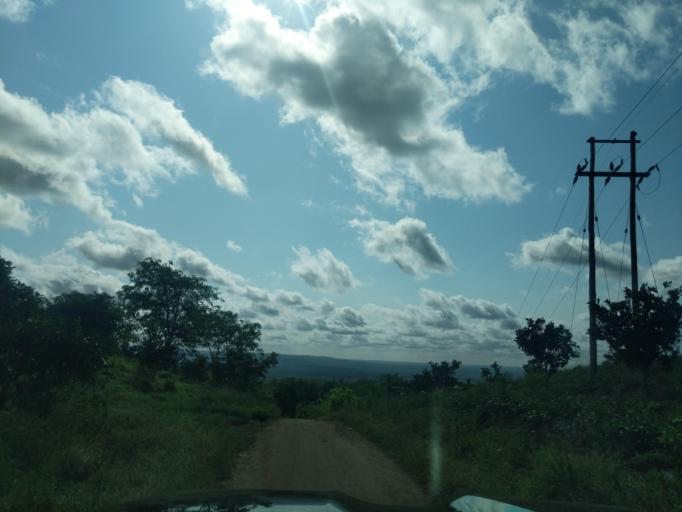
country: TZ
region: Tanga
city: Muheza
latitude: -5.4217
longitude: 38.6395
